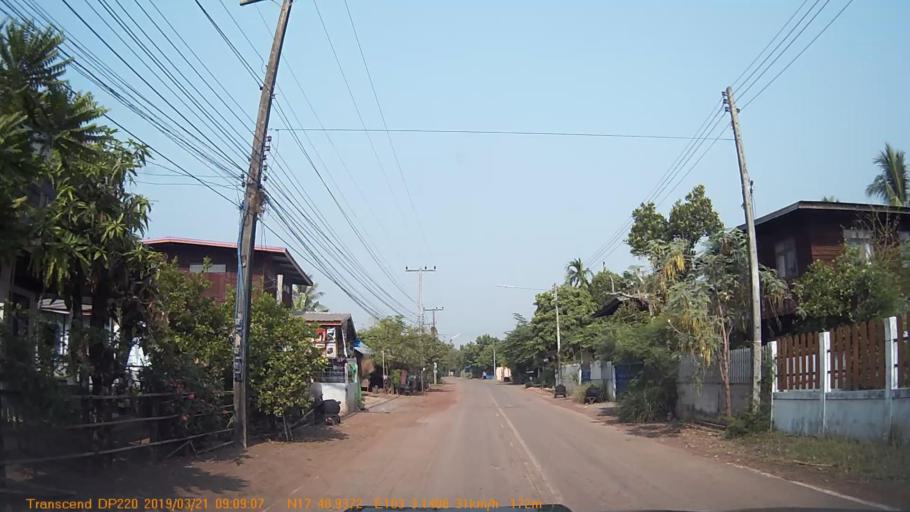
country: TH
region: Changwat Udon Thani
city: Phibun Rak
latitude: 17.6822
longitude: 103.0520
